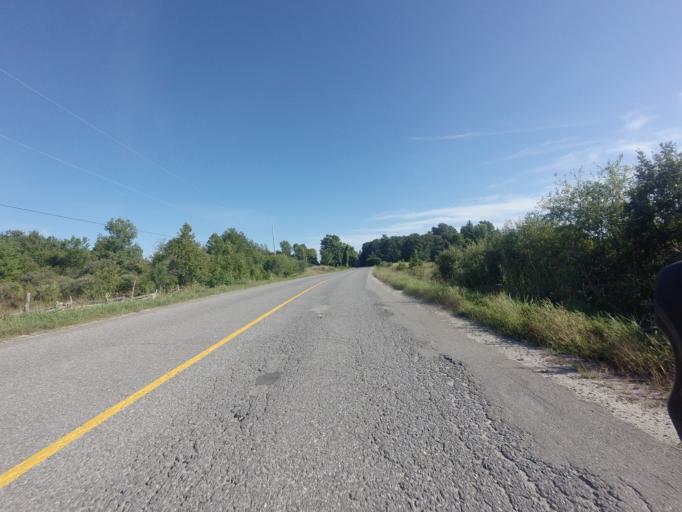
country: CA
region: Ontario
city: Perth
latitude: 44.9204
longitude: -76.3565
